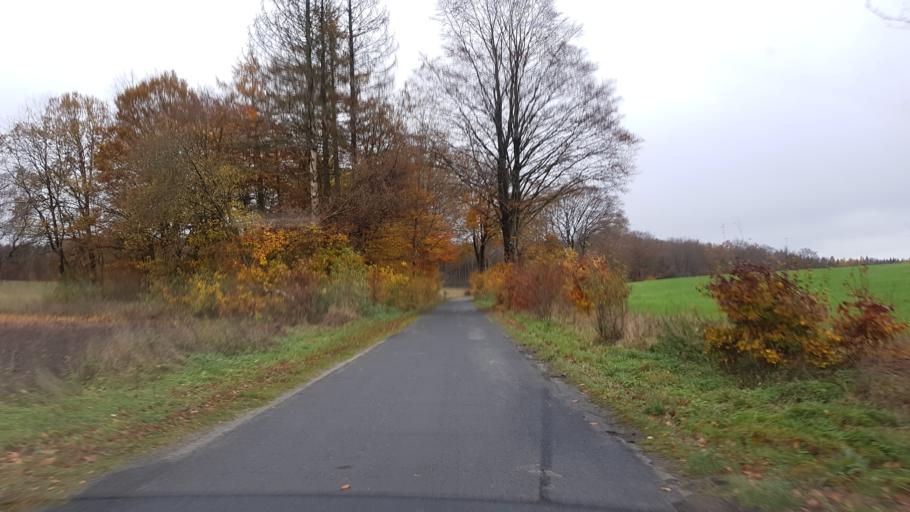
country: PL
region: West Pomeranian Voivodeship
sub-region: Powiat koszalinski
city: Polanow
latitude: 54.0848
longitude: 16.5943
